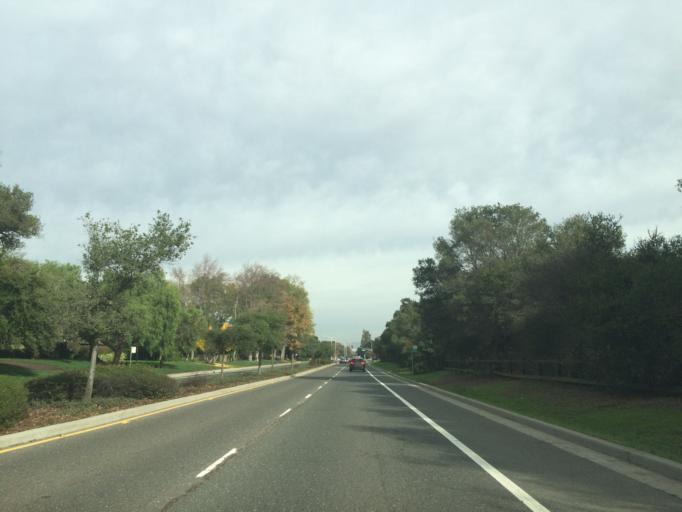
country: US
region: California
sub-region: San Mateo County
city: West Menlo Park
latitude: 37.4328
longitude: -122.1844
